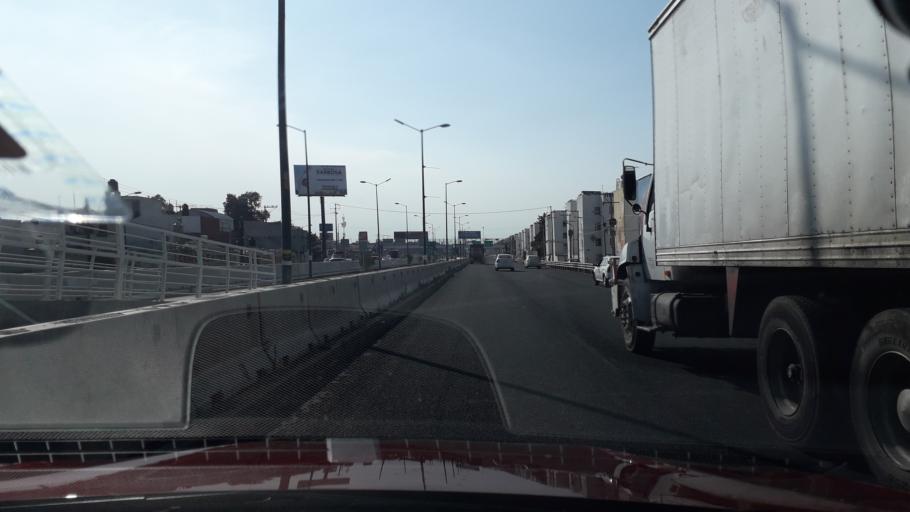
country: MX
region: Puebla
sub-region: Puebla
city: El Capulo (La Quebradora)
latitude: 18.9870
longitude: -98.2358
